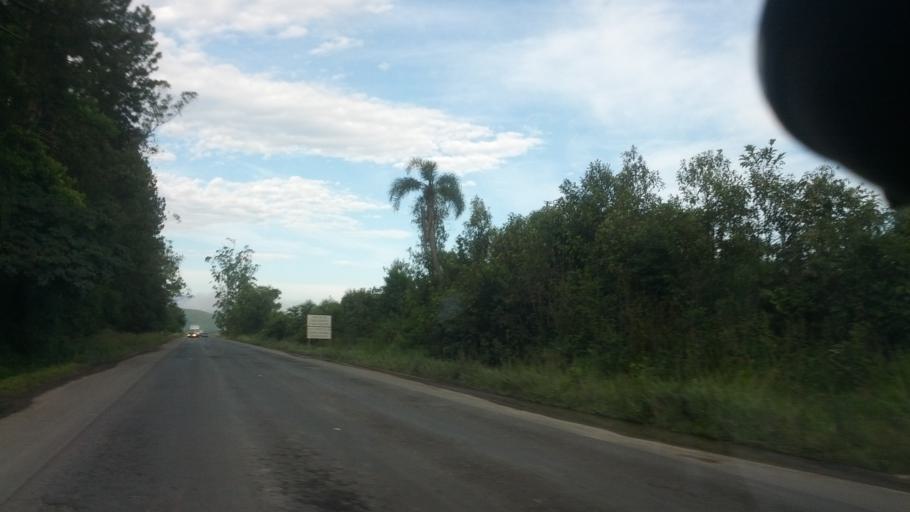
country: BR
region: Santa Catarina
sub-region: Otacilio Costa
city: Otacilio Costa
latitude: -27.2480
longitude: -49.9723
